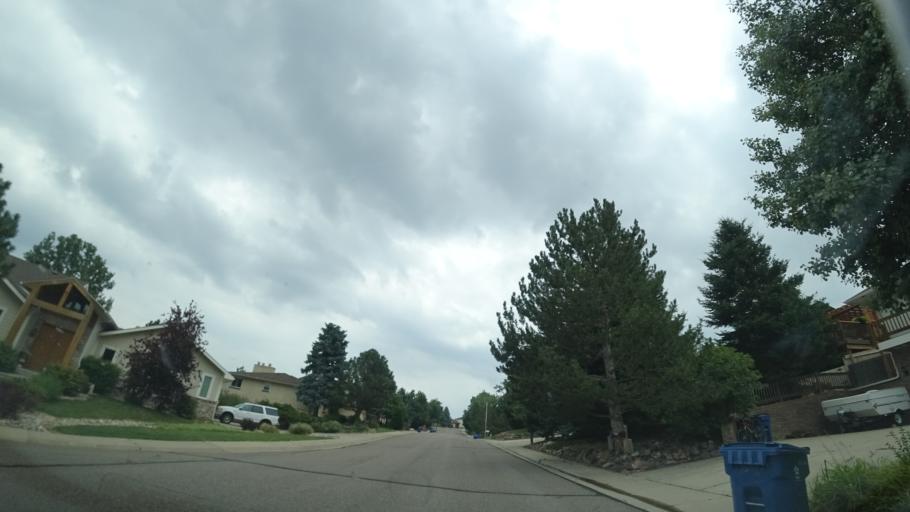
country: US
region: Colorado
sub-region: Jefferson County
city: West Pleasant View
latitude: 39.7064
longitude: -105.1600
